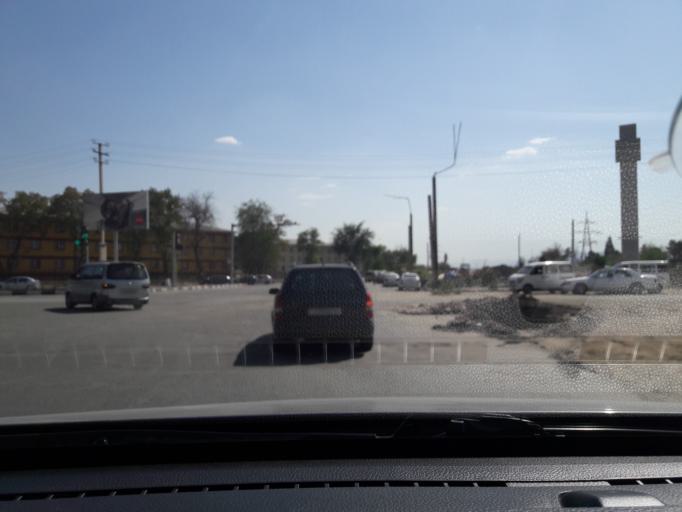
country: TJ
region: Dushanbe
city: Dushanbe
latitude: 38.5326
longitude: 68.7368
